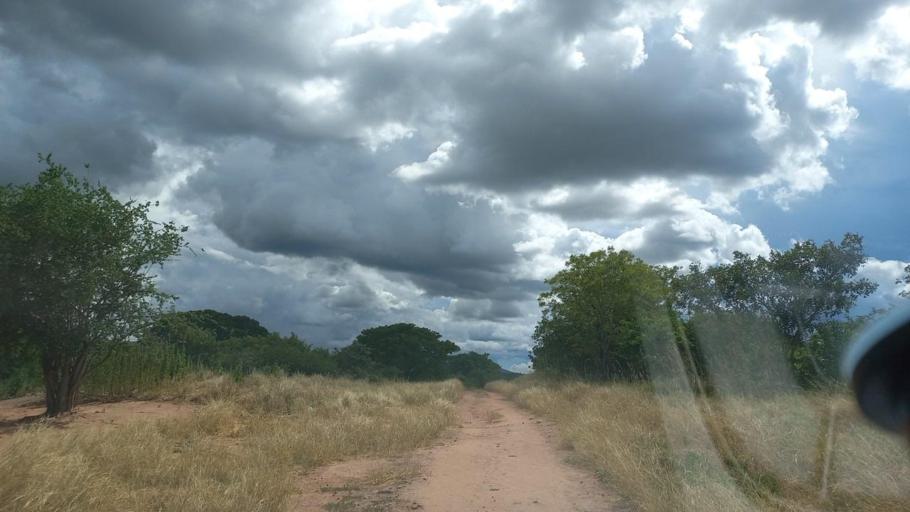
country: ZM
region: Lusaka
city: Luangwa
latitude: -15.6413
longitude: 30.3820
